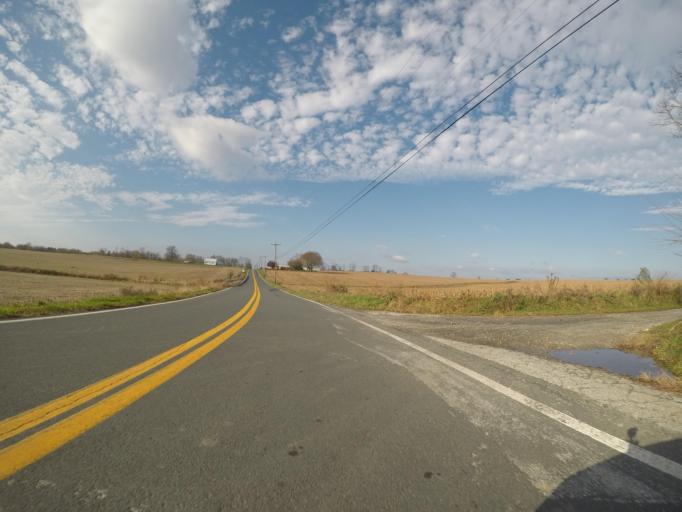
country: US
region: Maryland
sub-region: Carroll County
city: Hampstead
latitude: 39.5875
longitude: -76.8365
